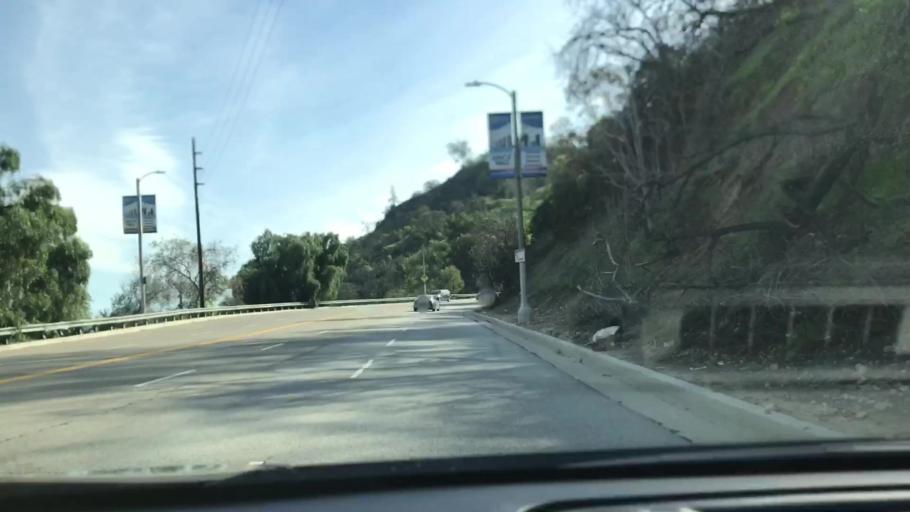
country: US
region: California
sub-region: Los Angeles County
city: Echo Park
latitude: 34.0910
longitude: -118.2408
